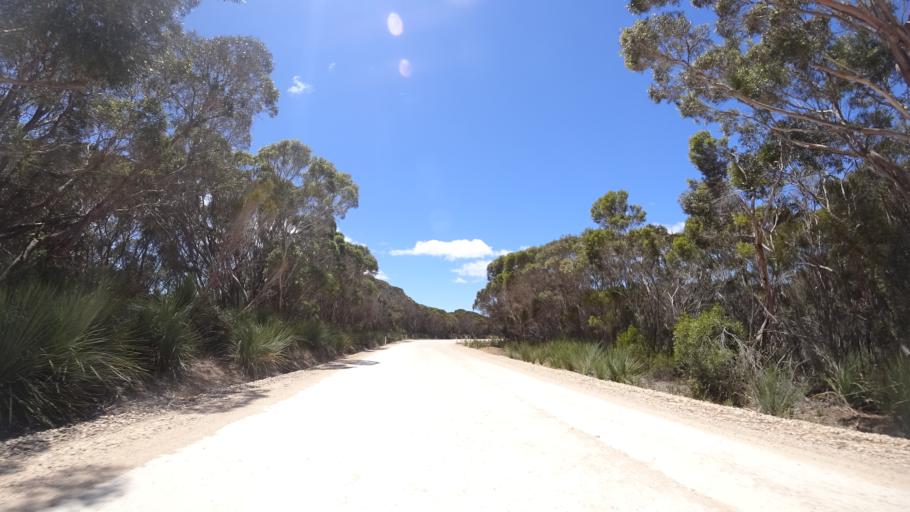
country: AU
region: South Australia
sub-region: Kangaroo Island
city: Kingscote
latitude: -35.8258
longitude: 137.9942
